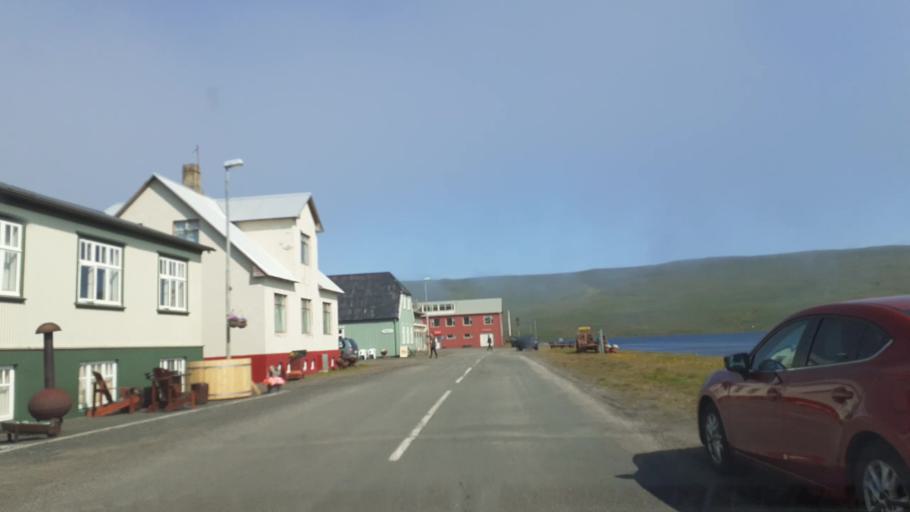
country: IS
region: West
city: Borgarnes
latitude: 65.2087
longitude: -21.0961
